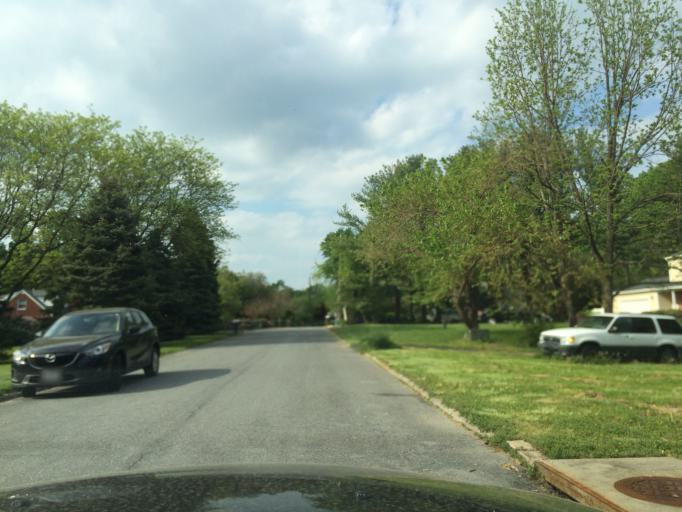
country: US
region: Maryland
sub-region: Howard County
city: Riverside
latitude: 39.1699
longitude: -76.9058
